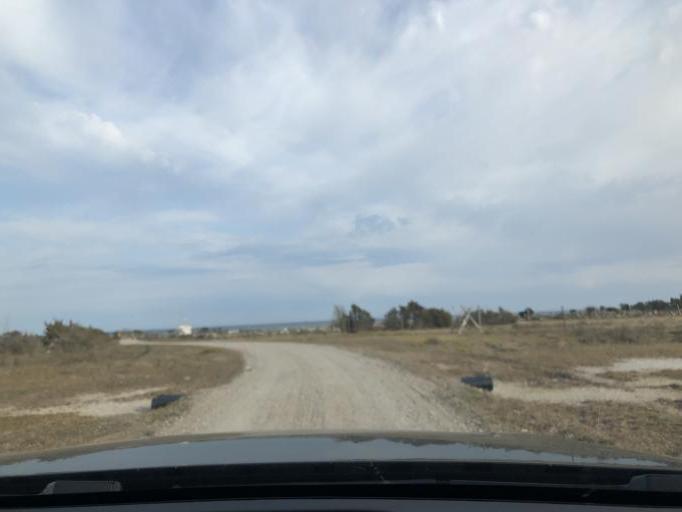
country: SE
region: Kalmar
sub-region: Morbylanga Kommun
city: Sodra Sandby
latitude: 56.5550
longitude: 16.6378
